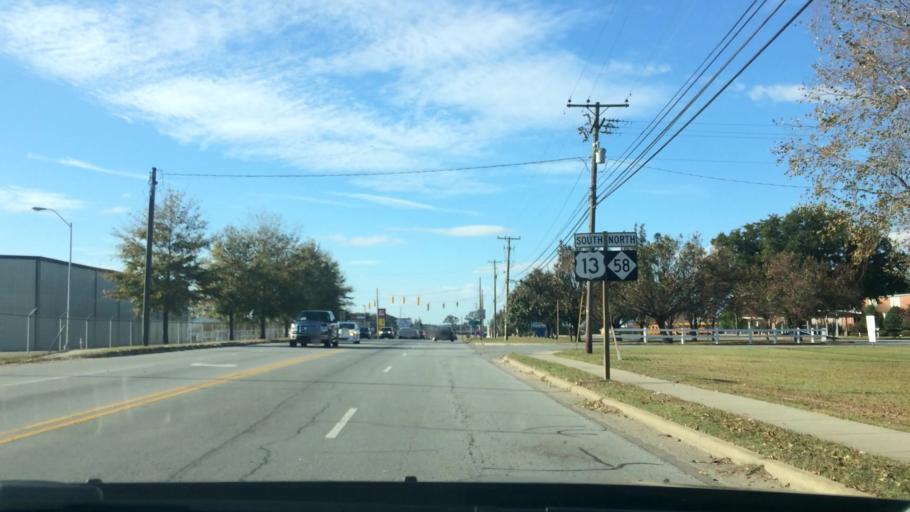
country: US
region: North Carolina
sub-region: Greene County
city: Snow Hill
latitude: 35.4527
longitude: -77.6857
